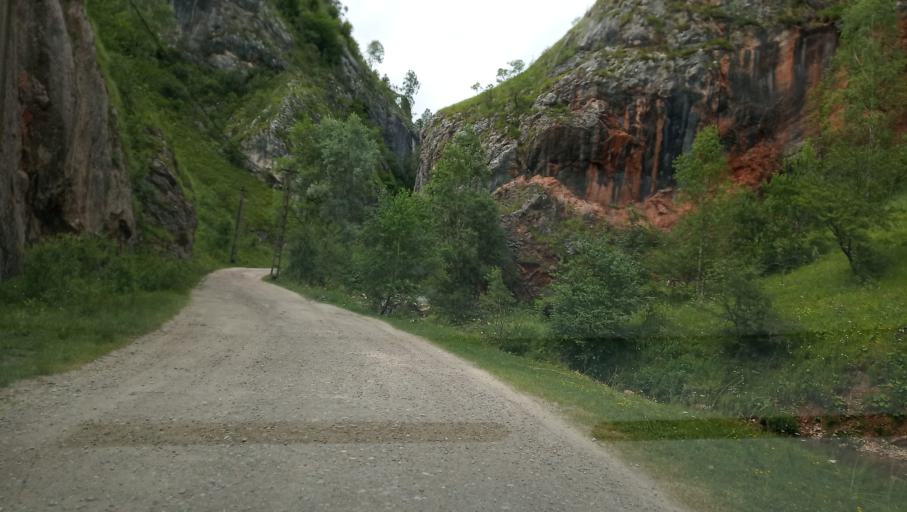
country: RO
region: Hunedoara
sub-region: Oras Petrila
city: Petrila
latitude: 45.4718
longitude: 23.4181
